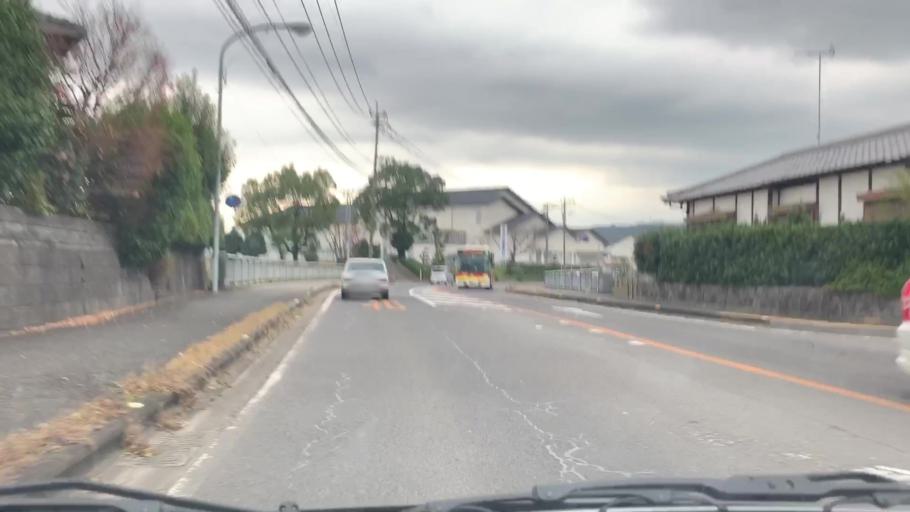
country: JP
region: Saga Prefecture
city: Kashima
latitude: 33.1317
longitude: 130.0614
